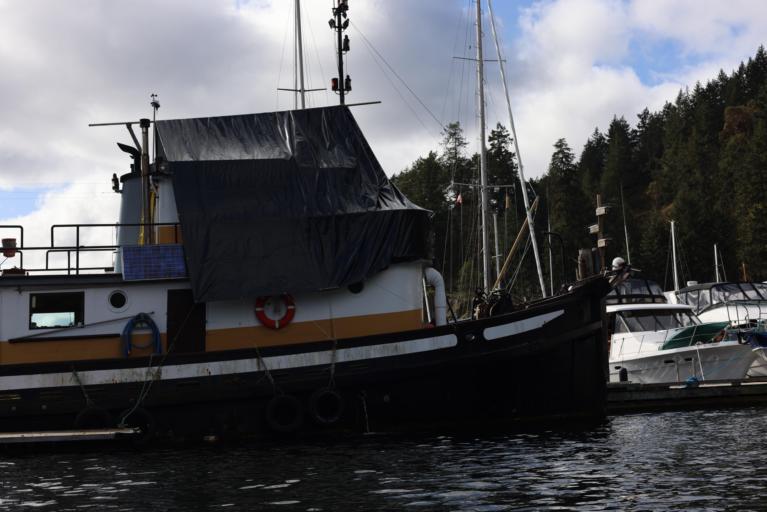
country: CA
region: British Columbia
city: Langford
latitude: 48.4983
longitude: -123.5522
